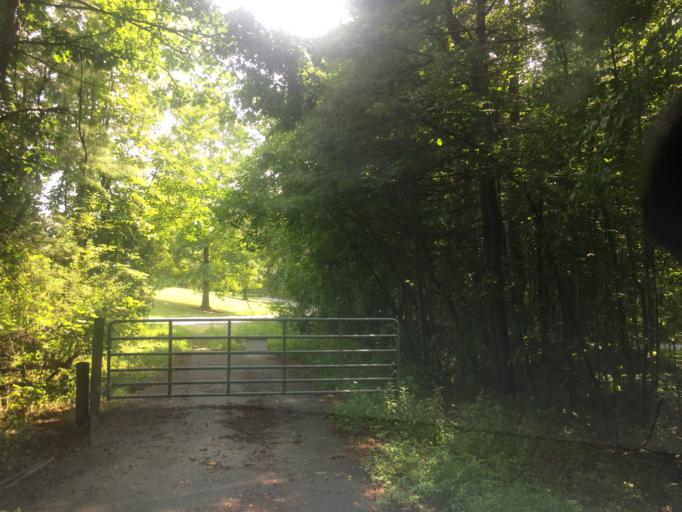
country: US
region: North Carolina
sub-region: Henderson County
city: Laurel Park
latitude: 35.3260
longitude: -82.4944
